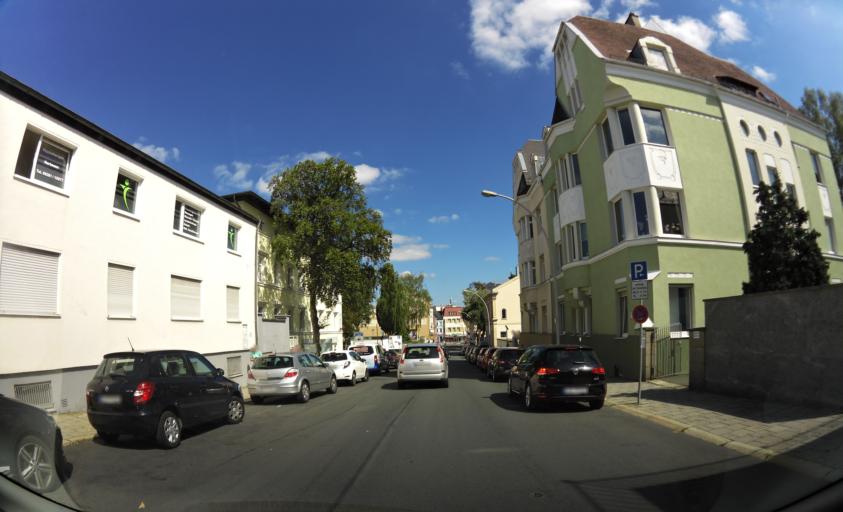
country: DE
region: Bavaria
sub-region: Upper Franconia
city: Hof
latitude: 50.3181
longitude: 11.9113
